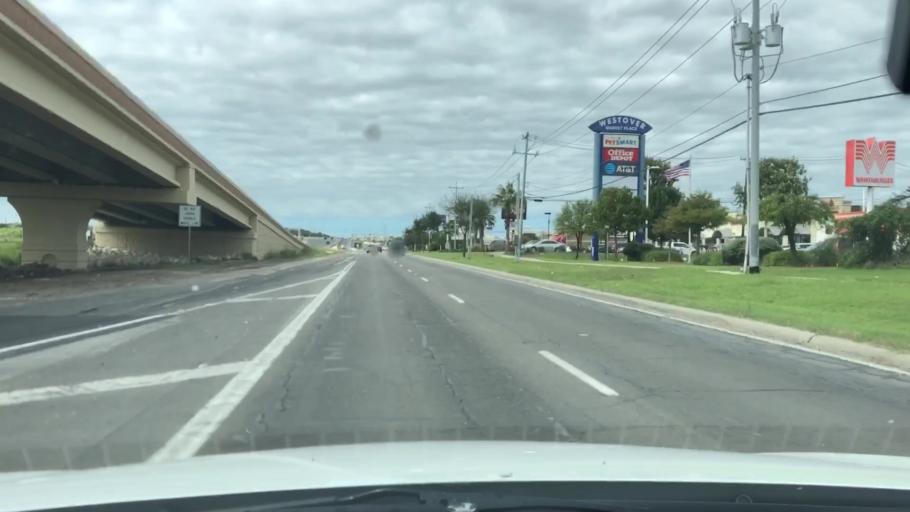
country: US
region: Texas
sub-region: Bexar County
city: Lackland Air Force Base
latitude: 29.4364
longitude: -98.6514
